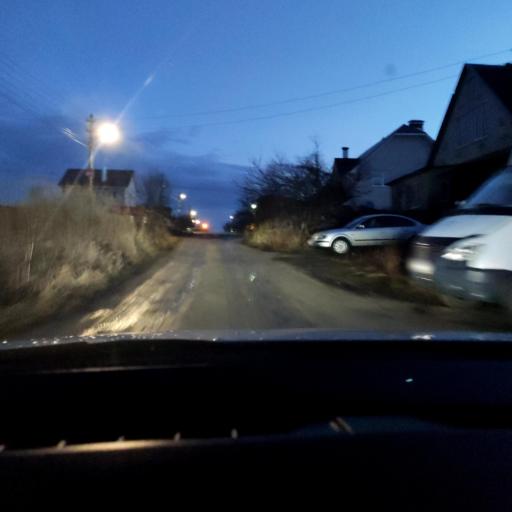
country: RU
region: Voronezj
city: Semiluki
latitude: 51.7133
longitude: 39.0210
